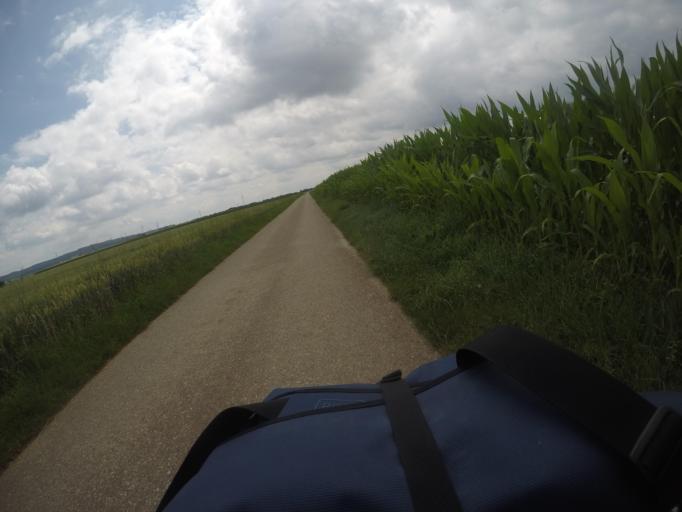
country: DE
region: Bavaria
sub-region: Swabia
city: Heimertingen
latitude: 48.0578
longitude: 10.1561
